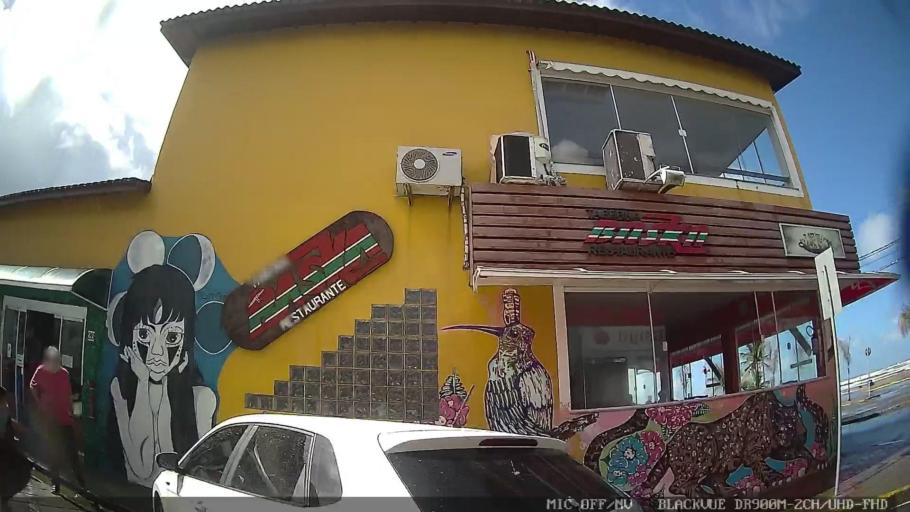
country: BR
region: Sao Paulo
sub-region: Itanhaem
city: Itanhaem
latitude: -24.1885
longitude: -46.8018
